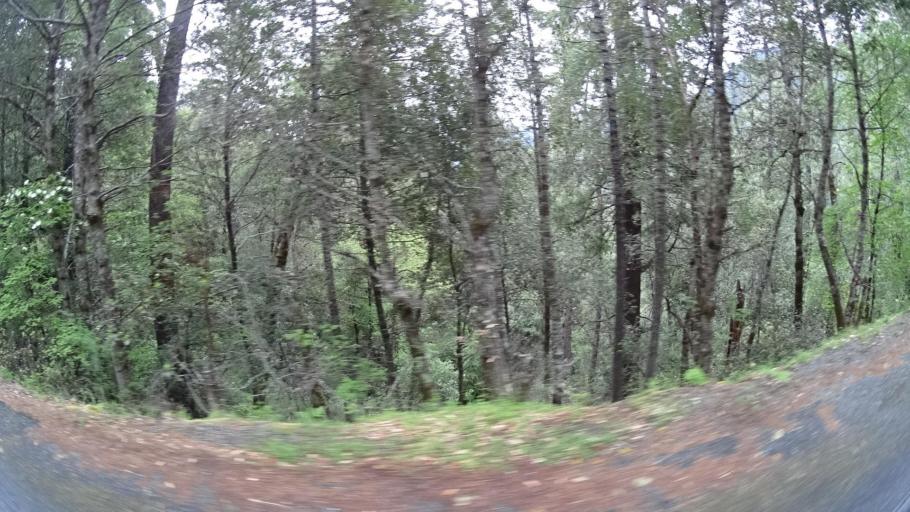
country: US
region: California
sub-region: Humboldt County
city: Willow Creek
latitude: 41.3533
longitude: -123.5124
